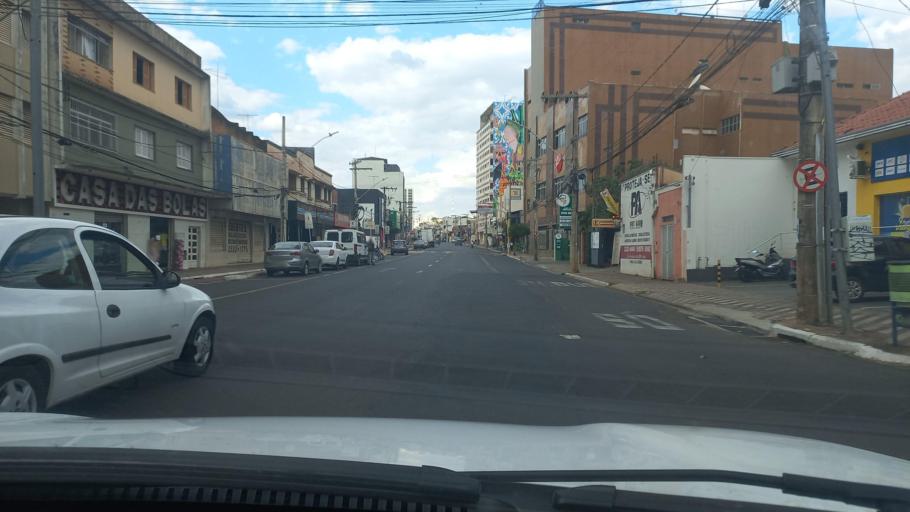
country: BR
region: Minas Gerais
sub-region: Uberaba
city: Uberaba
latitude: -19.7476
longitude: -47.9357
